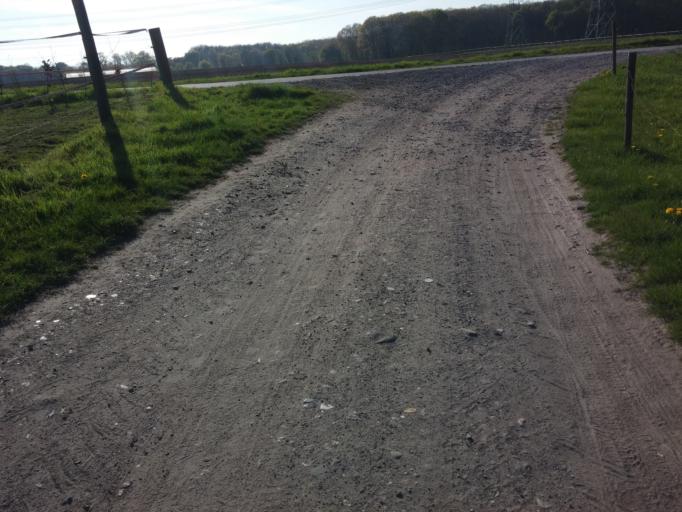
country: DE
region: North Rhine-Westphalia
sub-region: Regierungsbezirk Munster
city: Gladbeck
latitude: 51.6159
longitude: 7.0051
